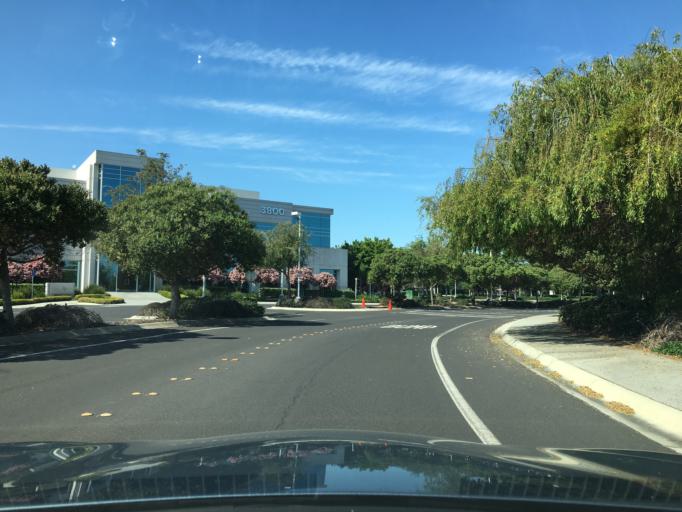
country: US
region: California
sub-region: San Mateo County
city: Redwood Shores
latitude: 37.5381
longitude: -122.2531
